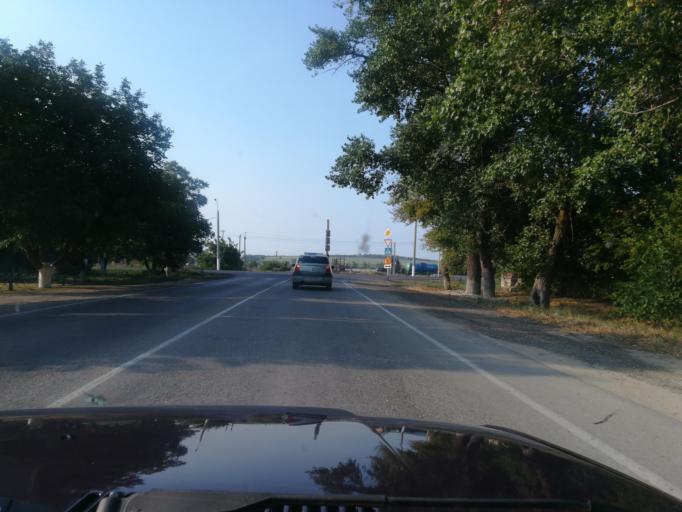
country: RU
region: Krasnodarskiy
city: Yurovka
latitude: 45.1178
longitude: 37.4220
